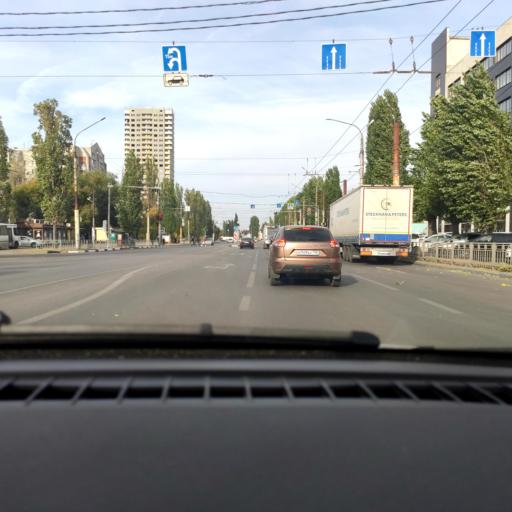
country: RU
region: Voronezj
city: Voronezh
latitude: 51.6998
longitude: 39.2735
